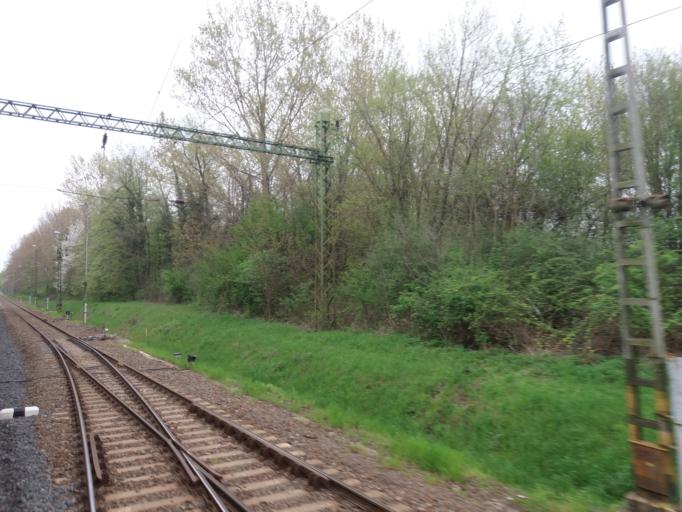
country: HU
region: Somogy
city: Balatonbereny
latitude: 46.6964
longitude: 17.2930
